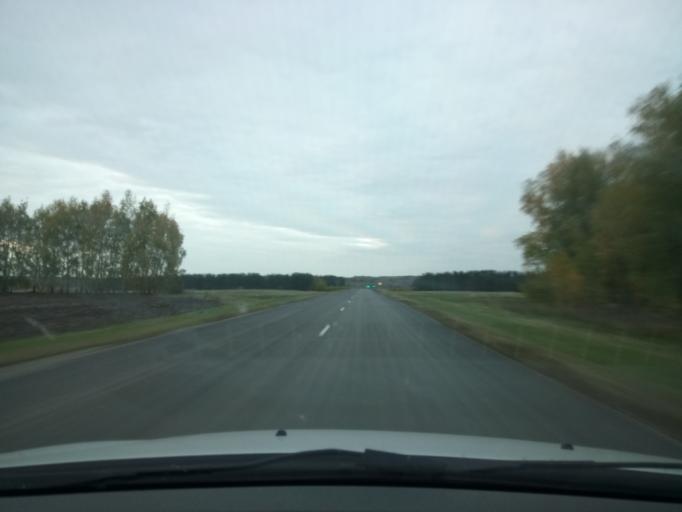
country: RU
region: Nizjnij Novgorod
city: Bol'shoye Murashkino
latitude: 55.7871
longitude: 44.7409
